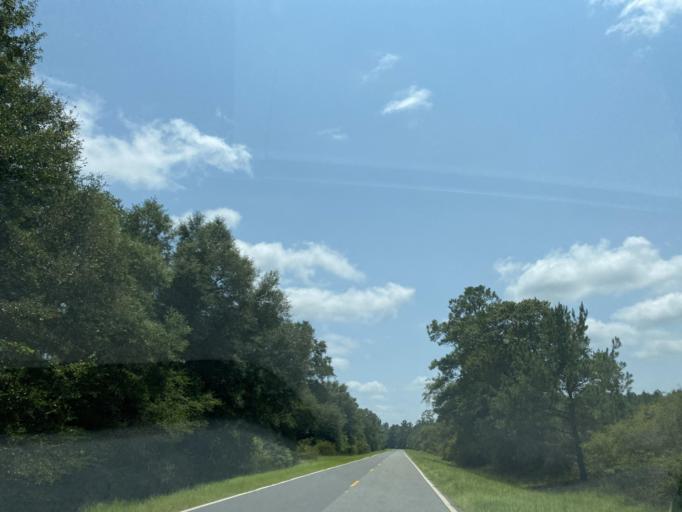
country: US
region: Georgia
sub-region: Telfair County
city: Lumber City
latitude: 31.9613
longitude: -82.7002
